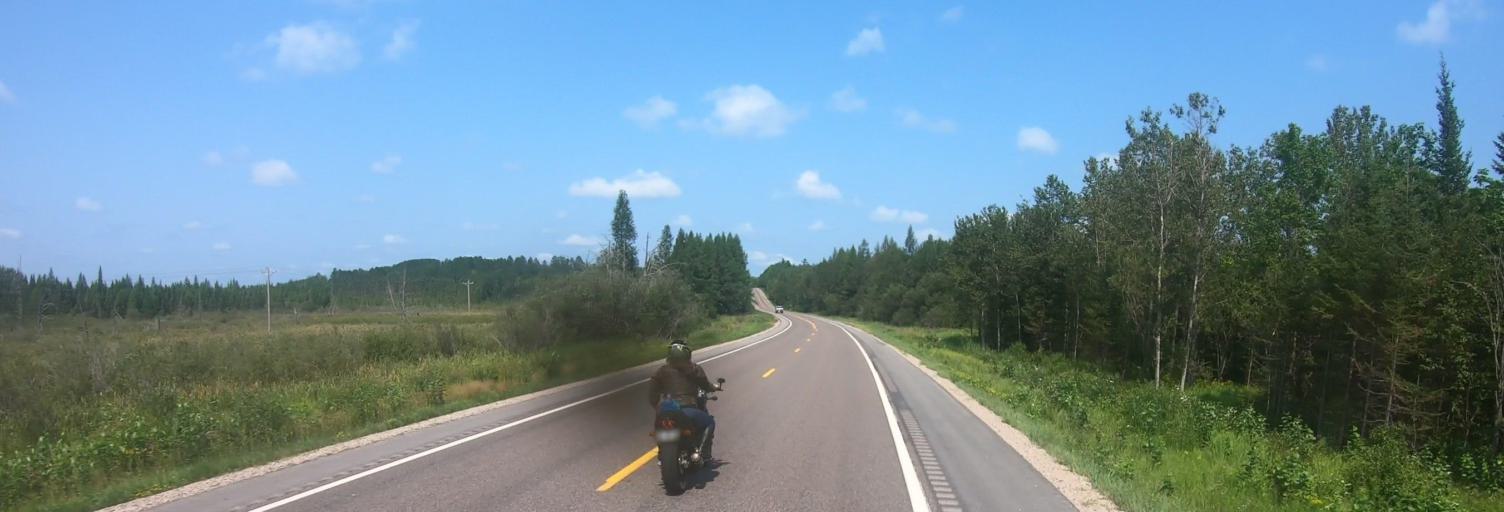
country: US
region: Minnesota
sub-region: Saint Louis County
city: Parkville
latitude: 48.1580
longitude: -92.5243
